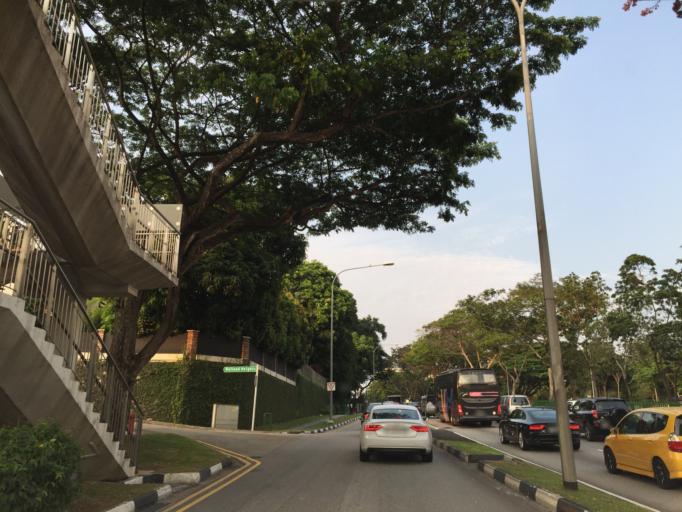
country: SG
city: Singapore
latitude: 1.3091
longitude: 103.8031
